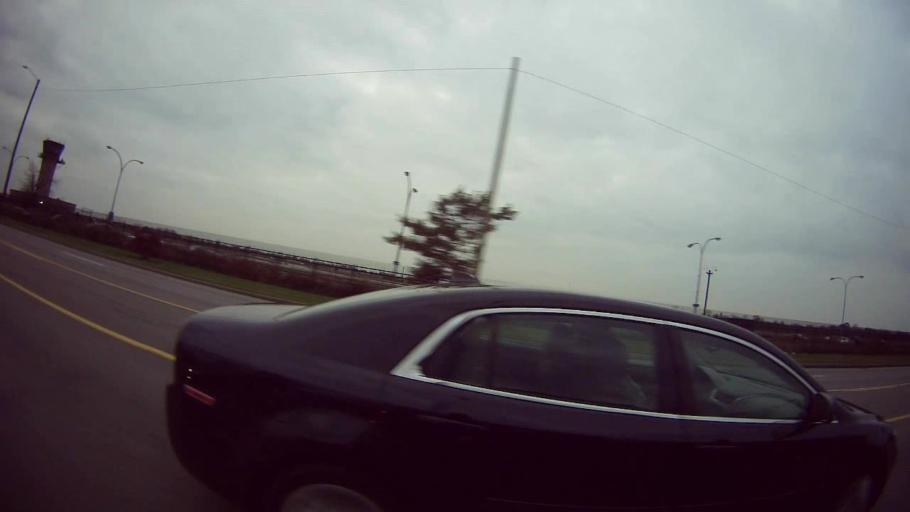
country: US
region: Michigan
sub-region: Wayne County
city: Hamtramck
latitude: 42.4110
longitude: -83.0053
